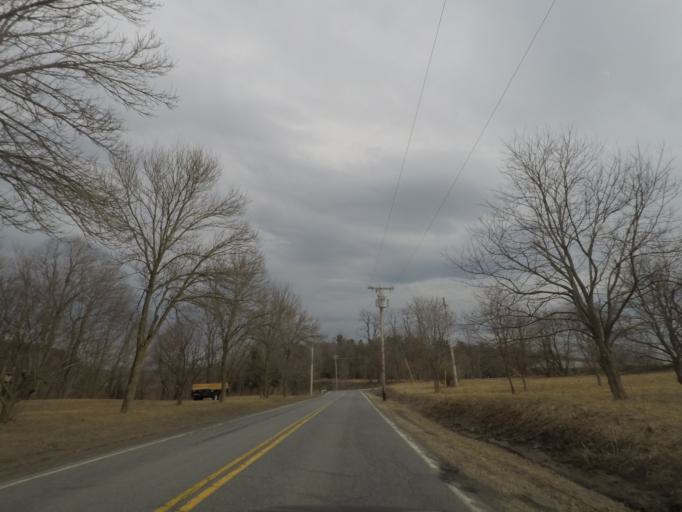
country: US
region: New York
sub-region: Washington County
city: Cambridge
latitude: 42.9585
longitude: -73.4547
